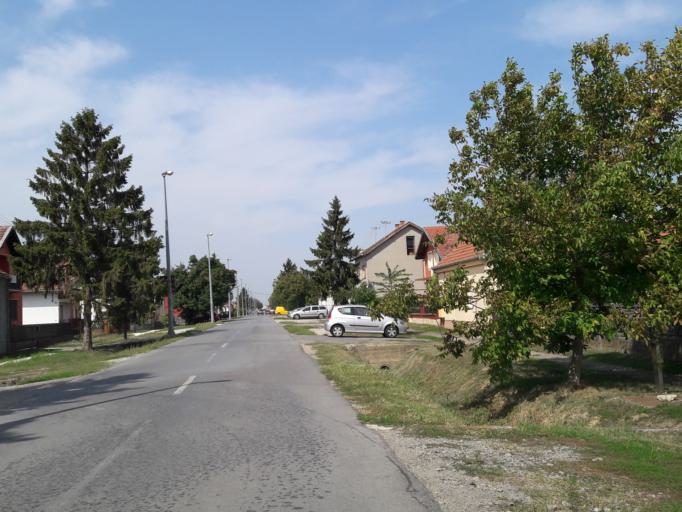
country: HR
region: Osjecko-Baranjska
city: Visnjevac
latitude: 45.5256
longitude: 18.6269
